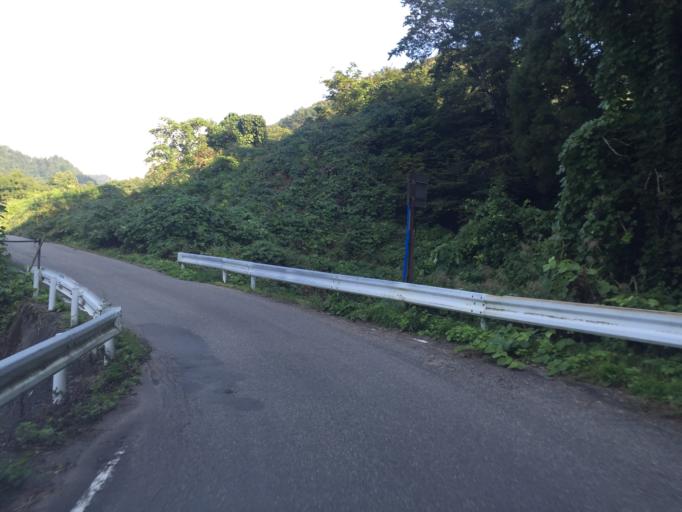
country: JP
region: Fukushima
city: Inawashiro
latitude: 37.4334
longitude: 139.9765
